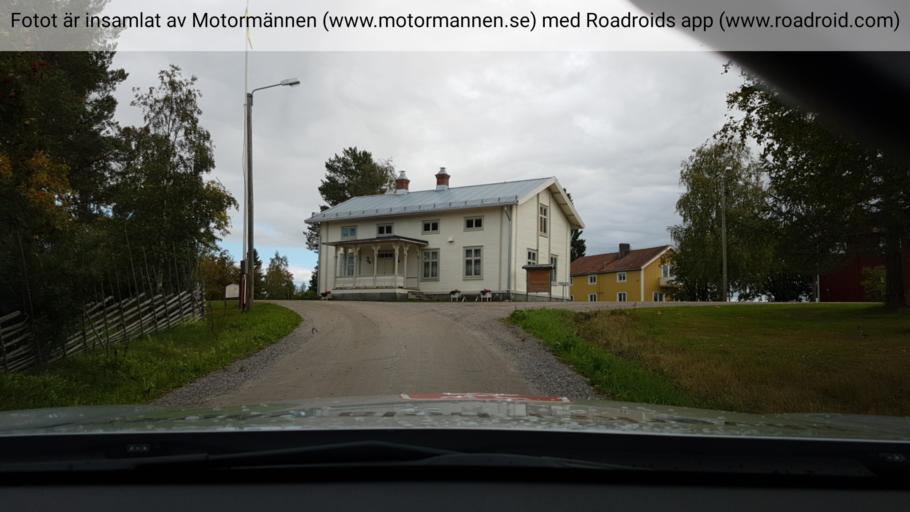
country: SE
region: Vaesterbotten
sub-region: Skelleftea Kommun
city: Byske
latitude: 65.1182
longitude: 21.2090
